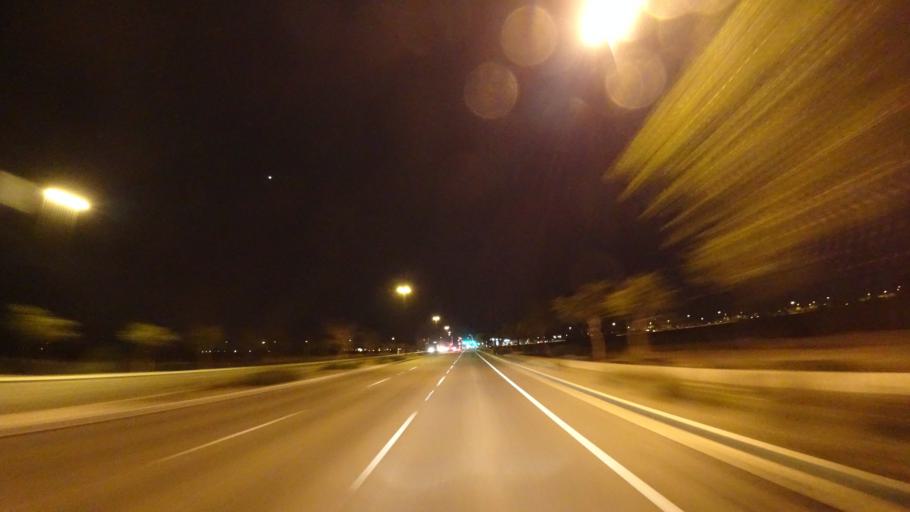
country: US
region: Arizona
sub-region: Maricopa County
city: Queen Creek
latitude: 33.2919
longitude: -111.6866
